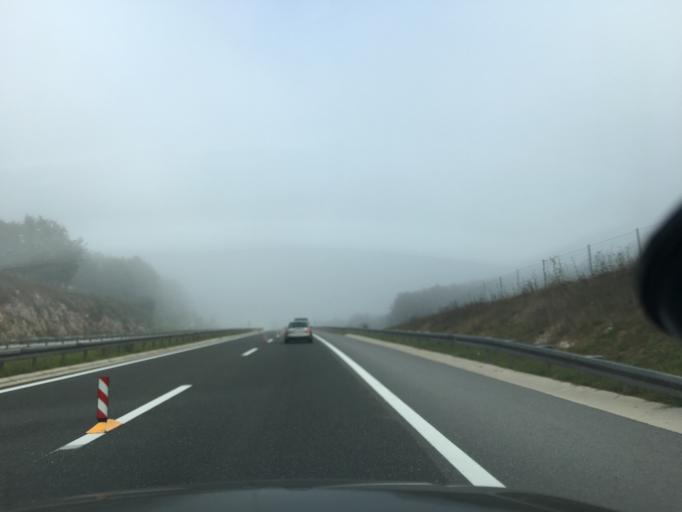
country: HR
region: Licko-Senjska
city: Otocac
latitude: 44.8768
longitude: 15.2057
